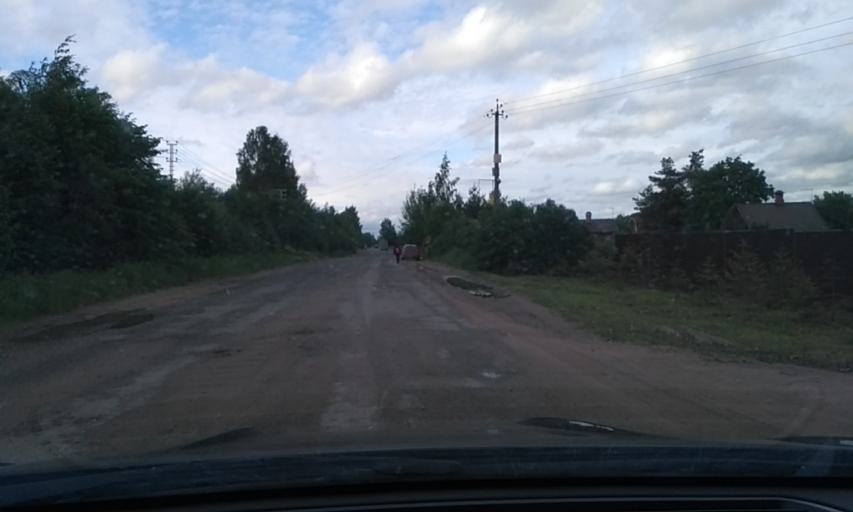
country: RU
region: Leningrad
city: Otradnoye
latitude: 59.7890
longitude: 30.7906
